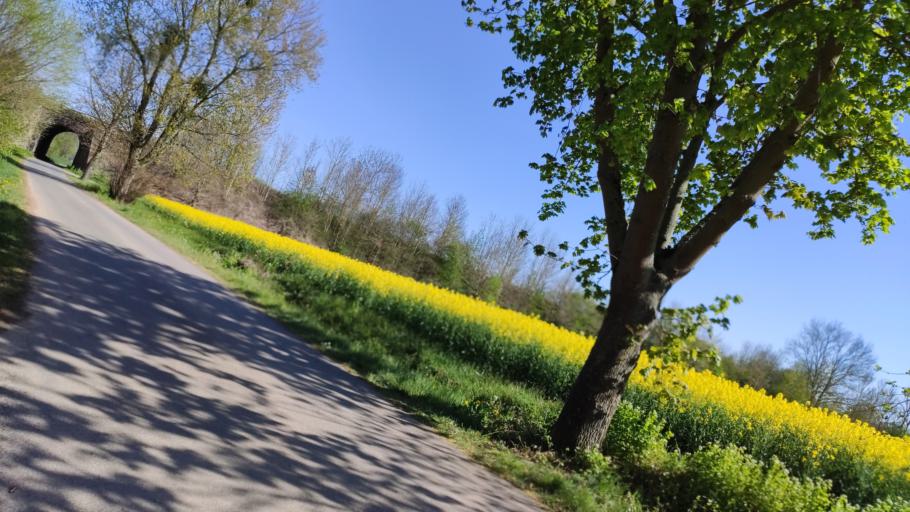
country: DE
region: Lower Saxony
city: Boffzen
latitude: 51.7414
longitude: 9.3600
